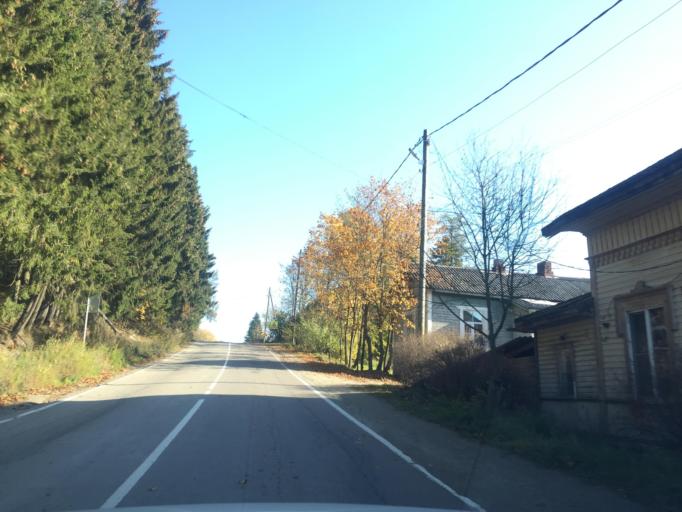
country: RU
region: Leningrad
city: Kuznechnoye
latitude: 61.2984
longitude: 29.8959
